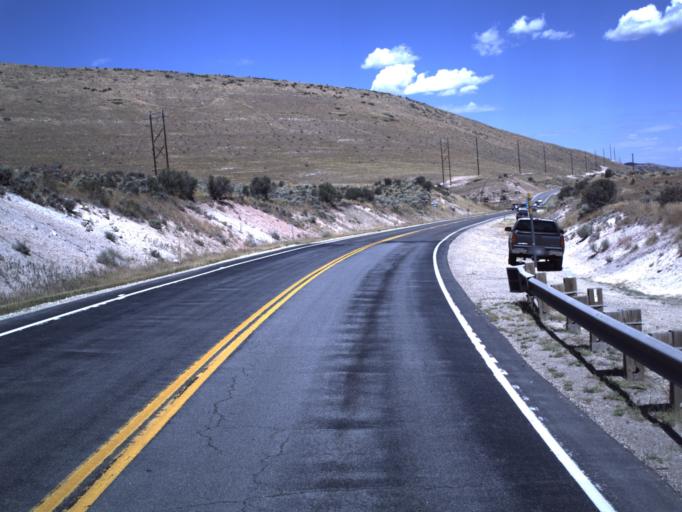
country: US
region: Utah
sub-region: Summit County
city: Oakley
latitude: 40.7726
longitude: -111.4074
